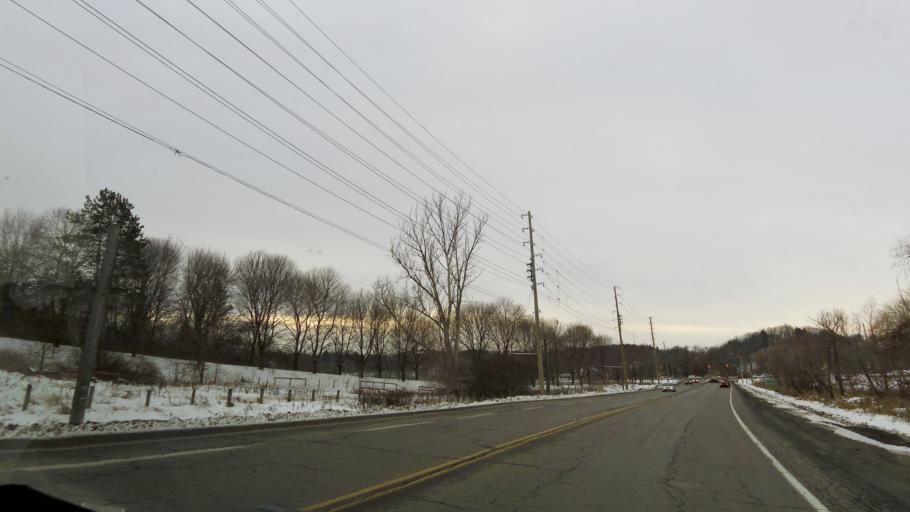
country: CA
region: Ontario
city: Vaughan
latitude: 43.8248
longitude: -79.6282
